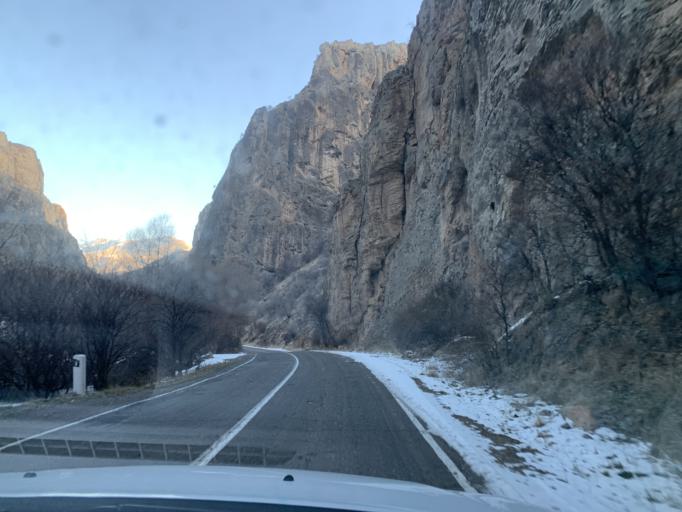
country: AM
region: Vayots' Dzori Marz
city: Areni
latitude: 39.7214
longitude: 45.2047
